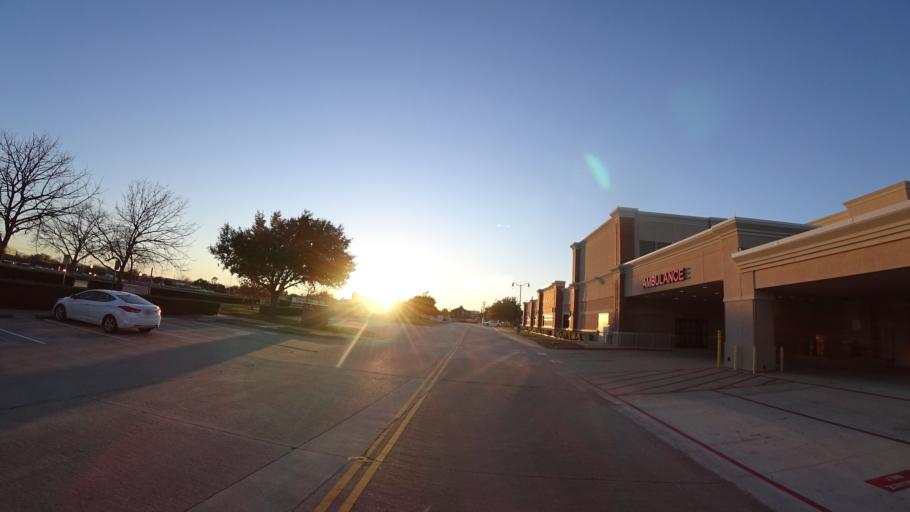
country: US
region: Texas
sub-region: Denton County
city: Lewisville
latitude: 33.0446
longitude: -97.0049
